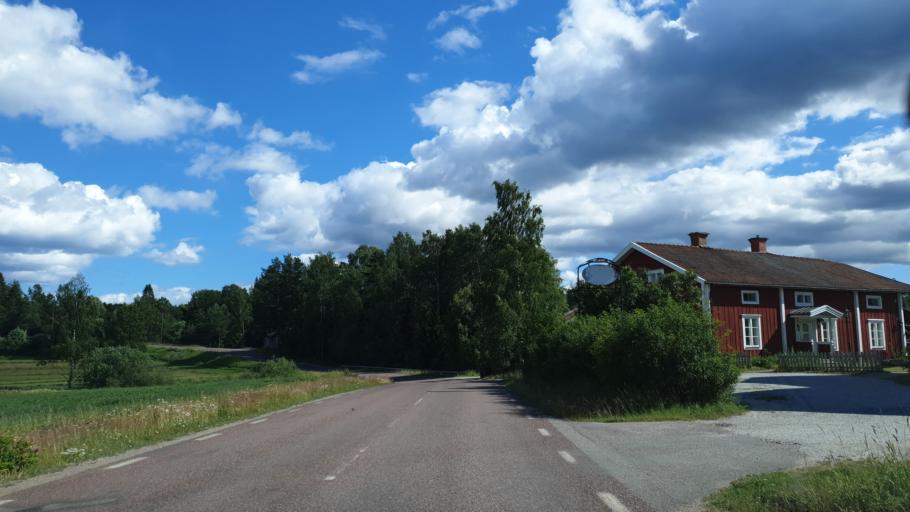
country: SE
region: Gaevleborg
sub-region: Nordanstigs Kommun
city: Bergsjoe
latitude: 62.0481
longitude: 17.2380
